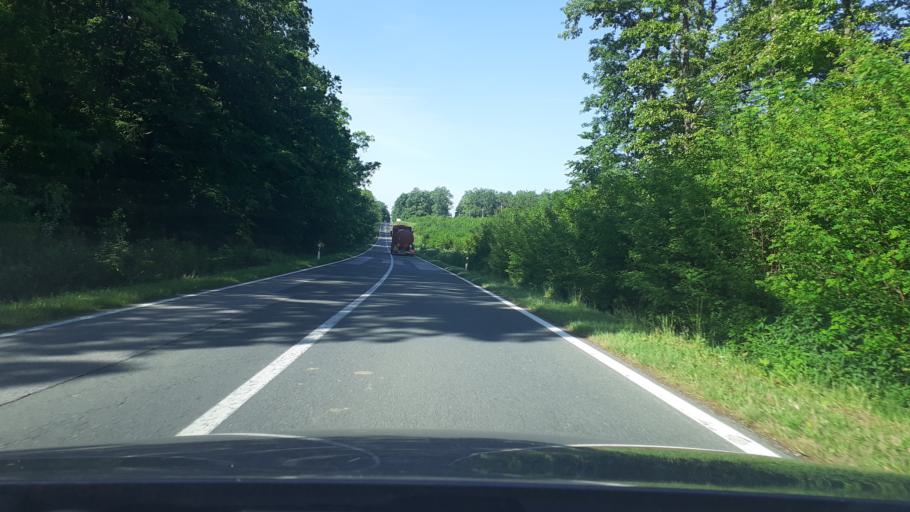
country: HR
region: Brodsko-Posavska
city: Batrina
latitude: 45.2091
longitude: 17.6841
